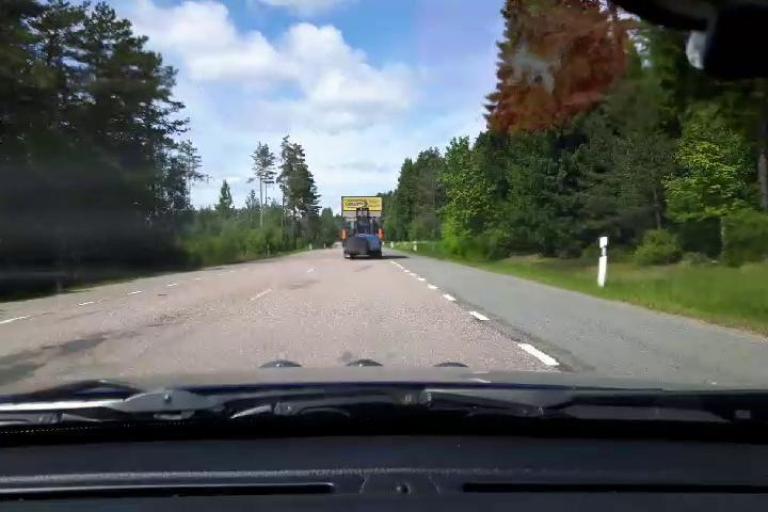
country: SE
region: Uppsala
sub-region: Osthammars Kommun
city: Bjorklinge
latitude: 60.1029
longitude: 17.5505
